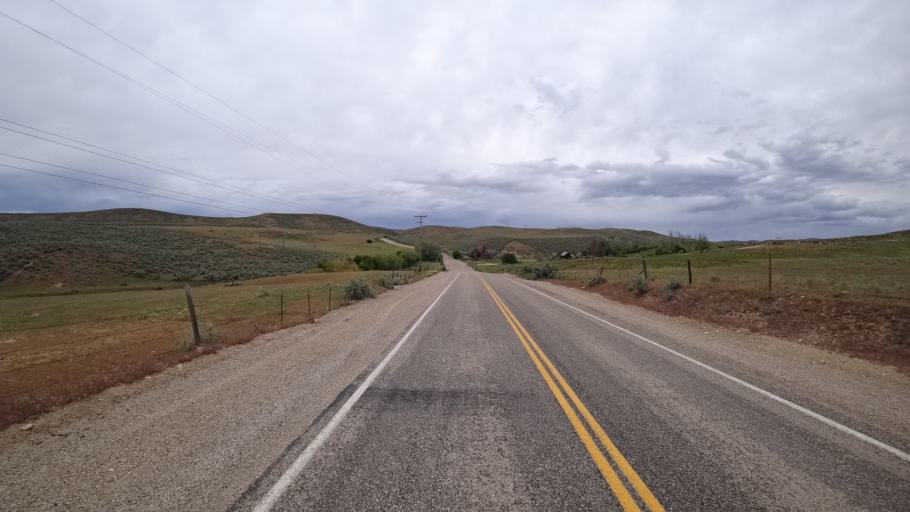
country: US
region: Idaho
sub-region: Ada County
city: Boise
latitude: 43.4808
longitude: -115.9973
